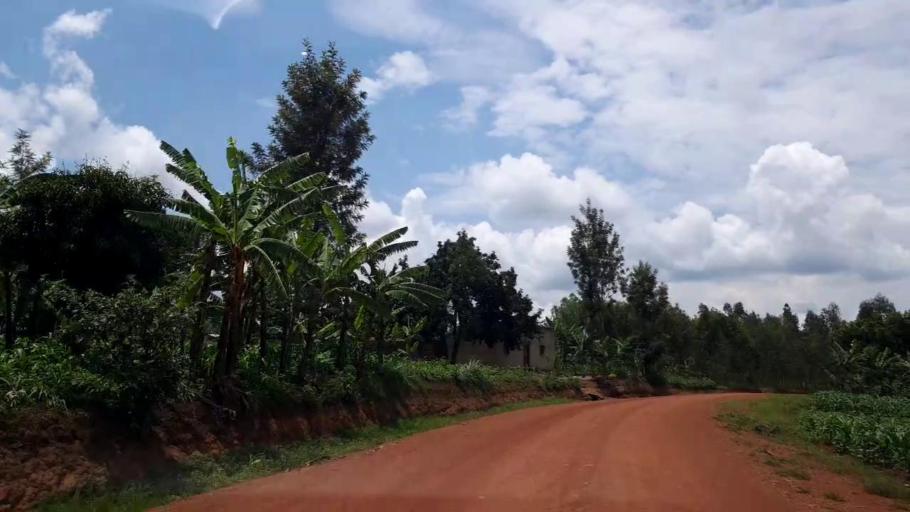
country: RW
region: Northern Province
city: Byumba
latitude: -1.5726
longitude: 30.3032
